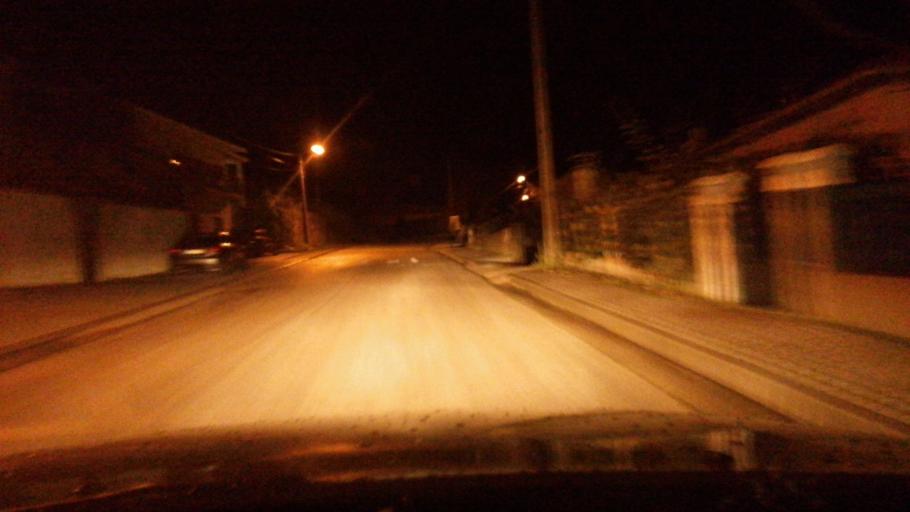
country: PT
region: Viseu
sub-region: Armamar
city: Armamar
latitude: 41.0604
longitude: -7.6452
